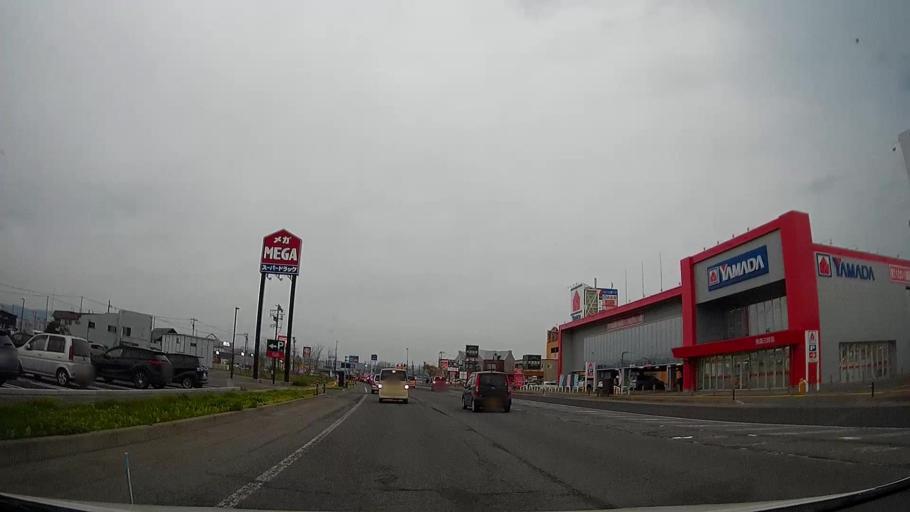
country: JP
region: Aomori
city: Aomori Shi
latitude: 40.8313
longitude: 140.7032
